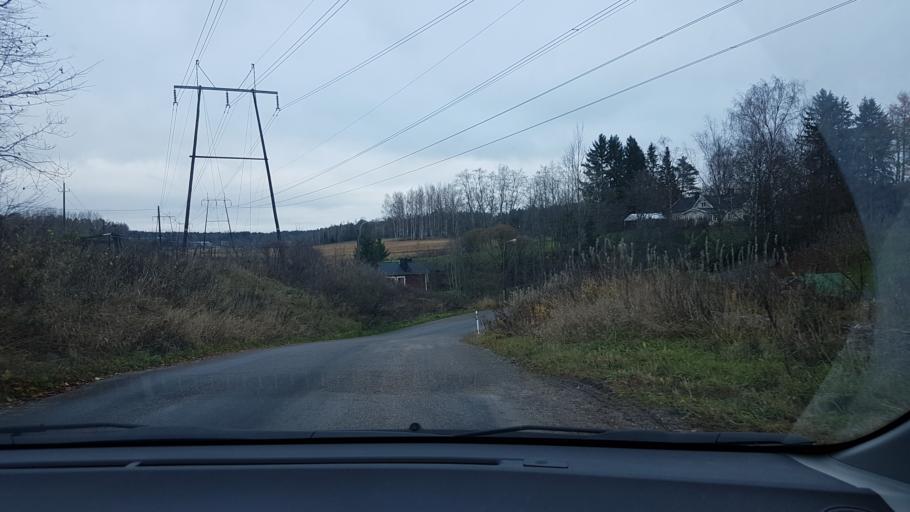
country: FI
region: Uusimaa
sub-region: Helsinki
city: Vantaa
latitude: 60.2827
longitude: 25.1395
